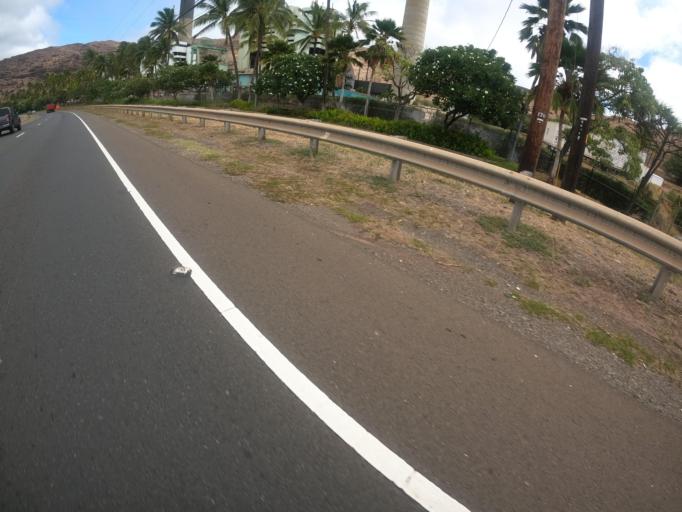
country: US
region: Hawaii
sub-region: Honolulu County
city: Makakilo
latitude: 21.3546
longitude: -158.1295
